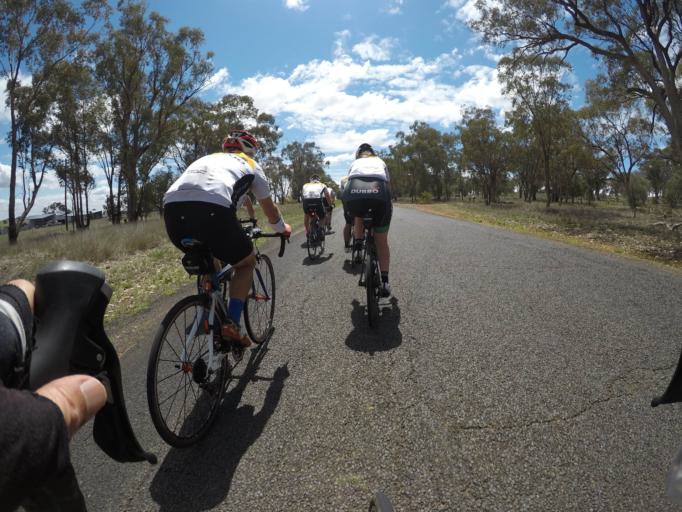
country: AU
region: New South Wales
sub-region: Dubbo Municipality
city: Dubbo
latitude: -32.3760
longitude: 148.5789
